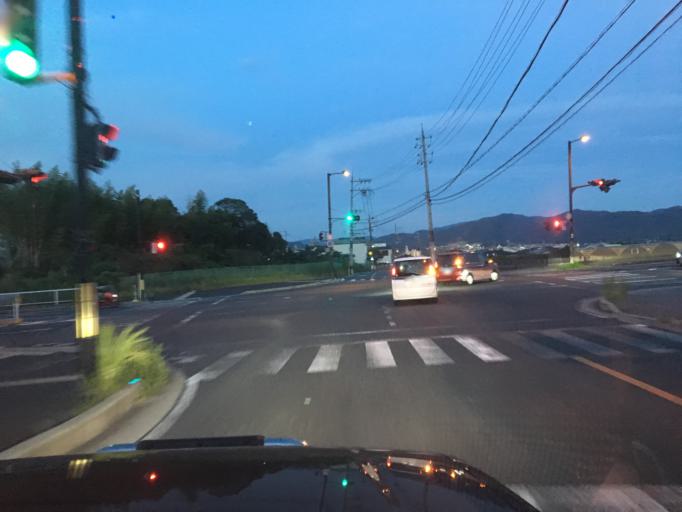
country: JP
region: Kyoto
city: Tanabe
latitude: 34.8182
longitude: 135.7612
